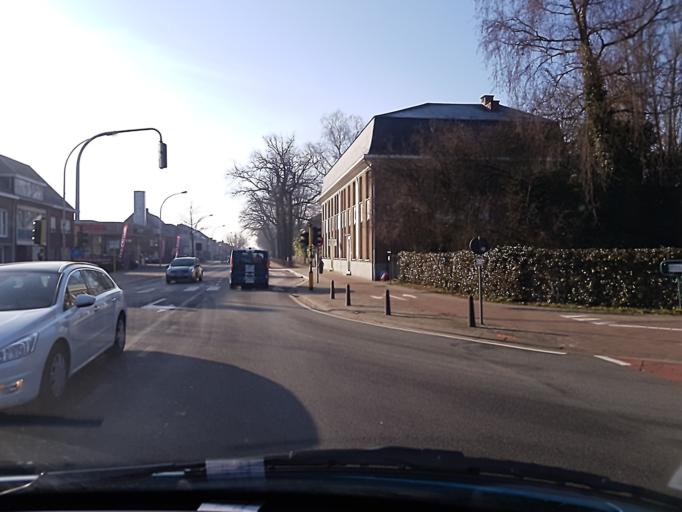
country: BE
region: Flanders
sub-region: Provincie Antwerpen
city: Zandhoven
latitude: 51.2714
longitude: 4.6457
